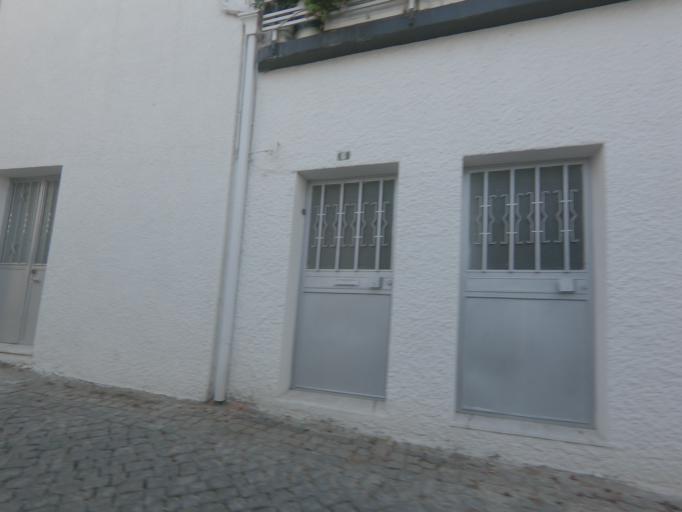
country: PT
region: Viseu
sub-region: Sao Joao da Pesqueira
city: Sao Joao da Pesqueira
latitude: 41.2262
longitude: -7.4660
